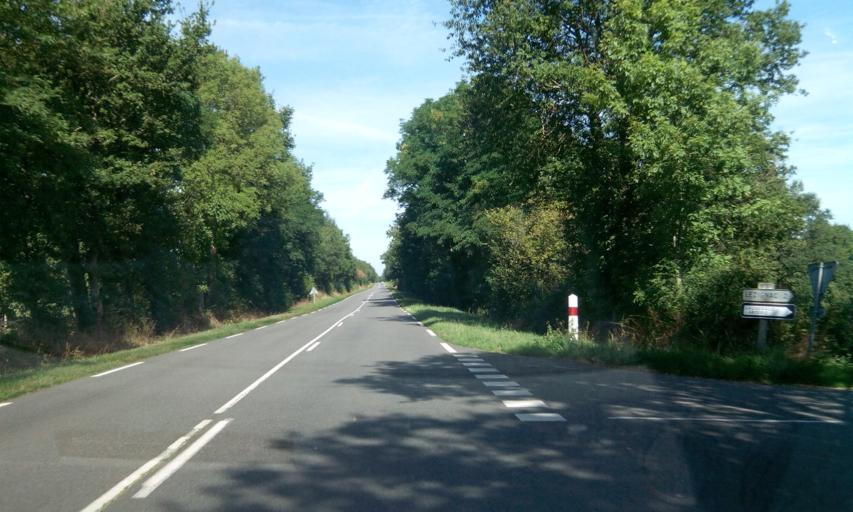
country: FR
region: Poitou-Charentes
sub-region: Departement de la Charente
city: Chabanais
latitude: 45.9466
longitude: 0.7230
